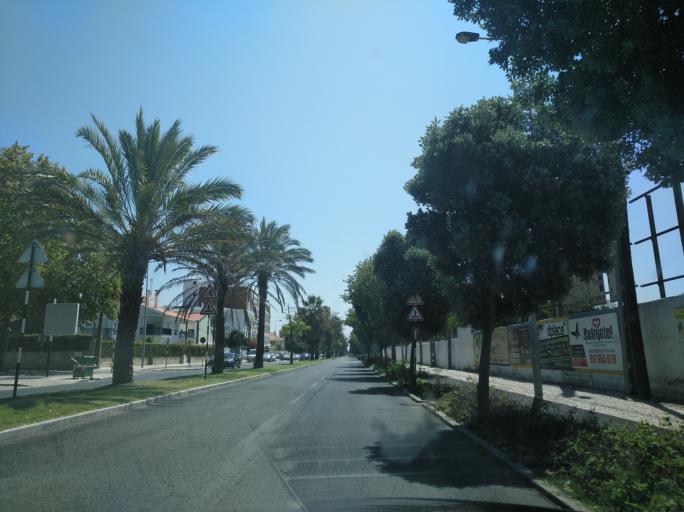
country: PT
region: Setubal
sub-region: Almada
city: Trafaria
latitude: 38.6634
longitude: -9.2434
